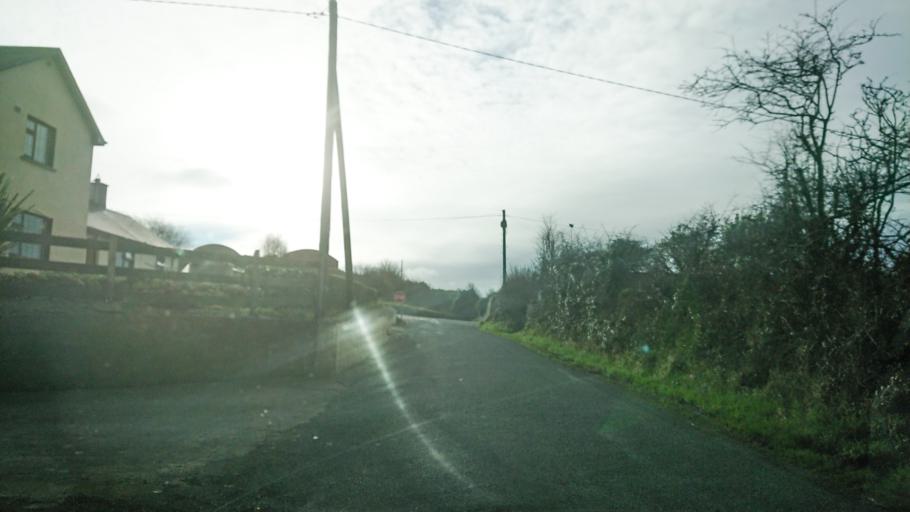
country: IE
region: Munster
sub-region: Waterford
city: Tra Mhor
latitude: 52.1564
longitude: -7.1902
